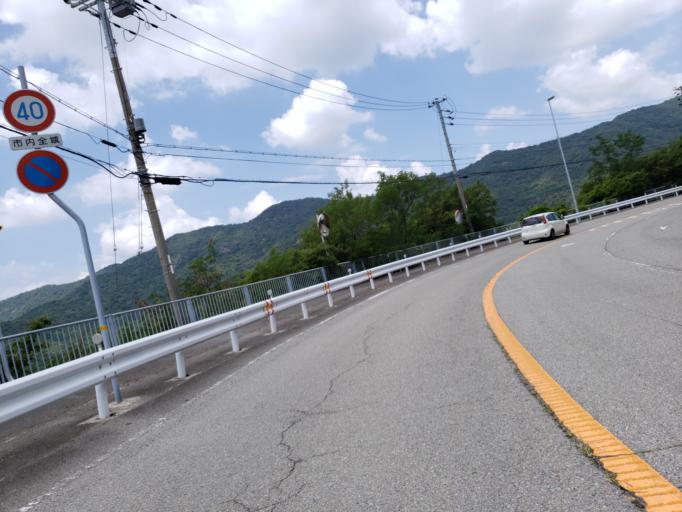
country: JP
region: Hyogo
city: Aioi
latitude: 34.7693
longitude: 134.5019
